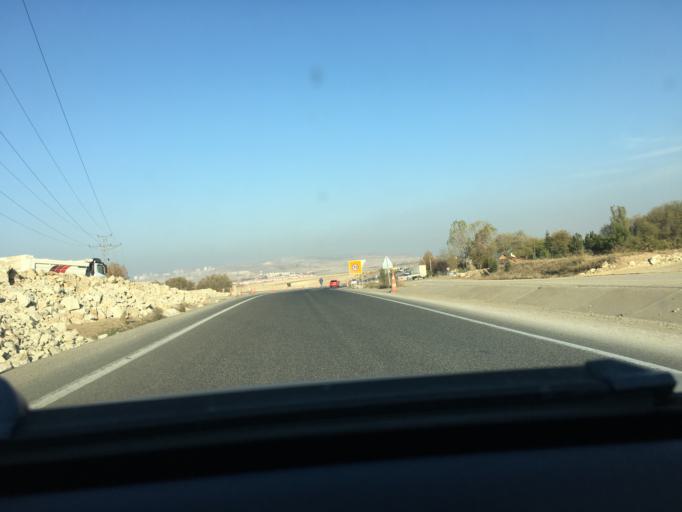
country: TR
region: Ankara
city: Temelli
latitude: 39.7424
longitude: 32.4095
